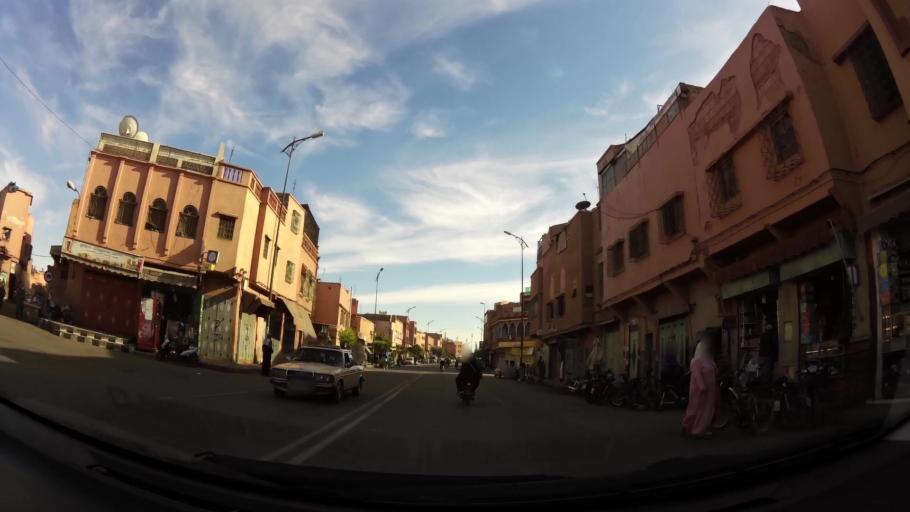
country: MA
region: Marrakech-Tensift-Al Haouz
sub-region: Marrakech
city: Marrakesh
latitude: 31.6223
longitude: -7.9709
